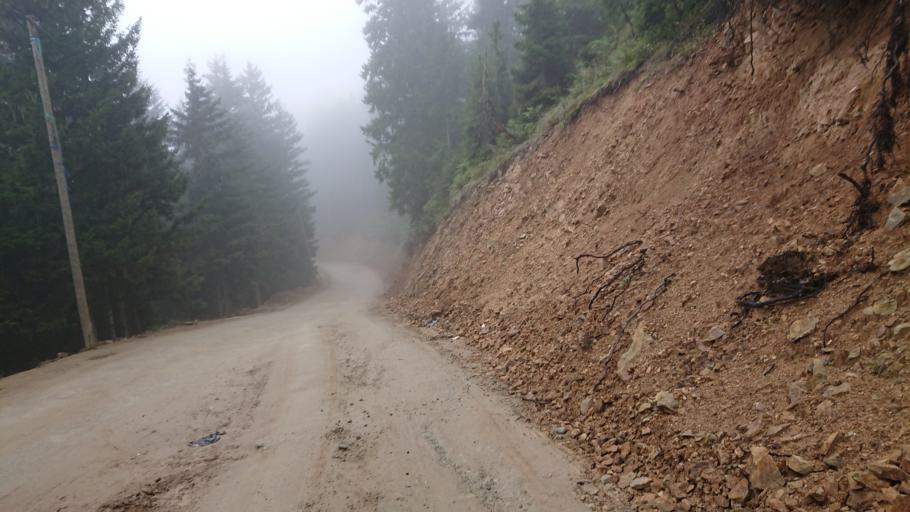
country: TR
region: Gumushane
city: Kurtun
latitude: 40.6711
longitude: 38.9999
